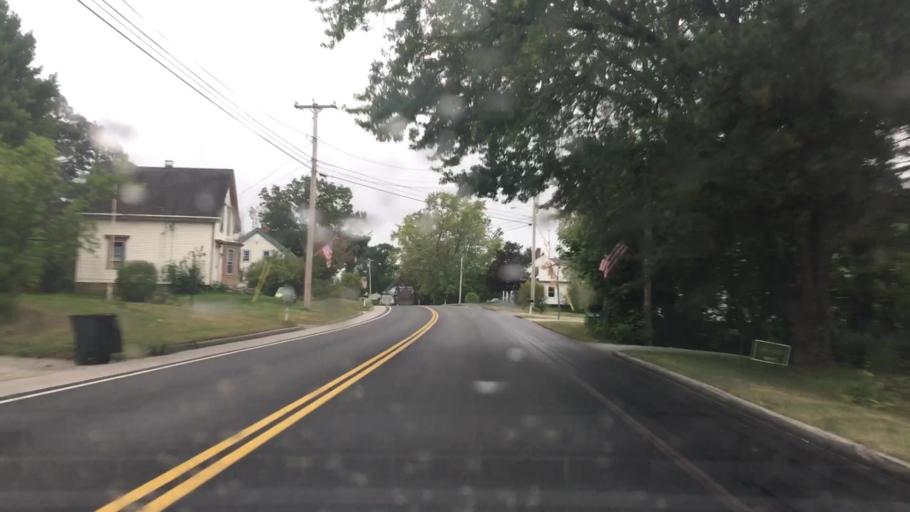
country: US
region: Maine
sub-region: Penobscot County
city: Orrington
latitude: 44.7506
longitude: -68.8046
